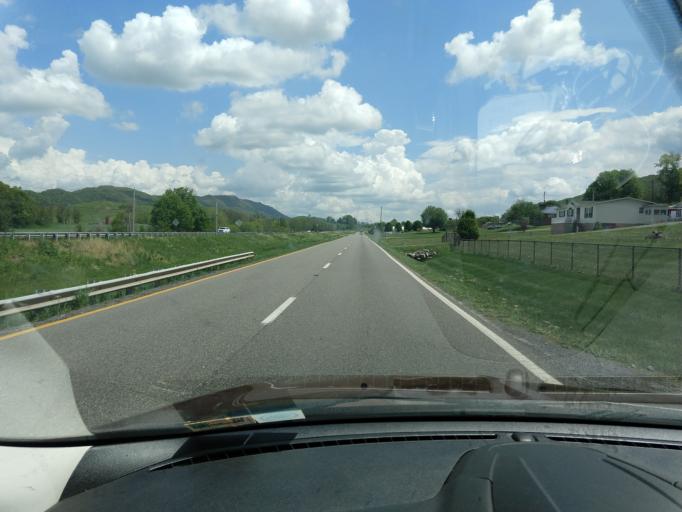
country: US
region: Virginia
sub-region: Russell County
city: Honaker
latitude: 36.9621
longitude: -81.9252
